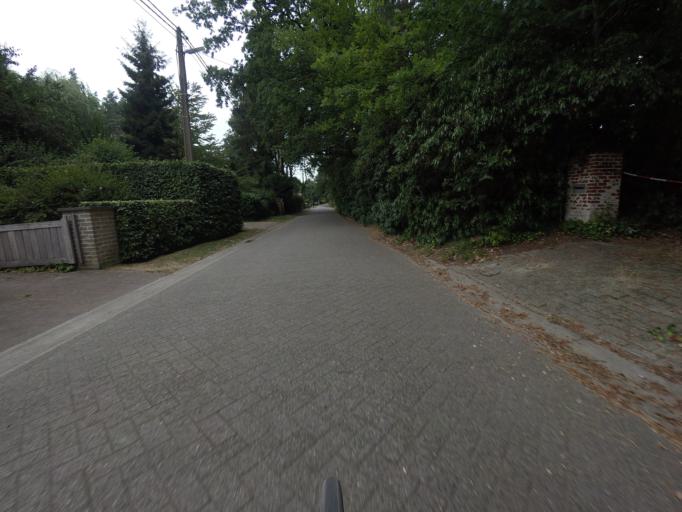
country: BE
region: Flanders
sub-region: Provincie Antwerpen
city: Schilde
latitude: 51.3011
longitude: 4.5884
